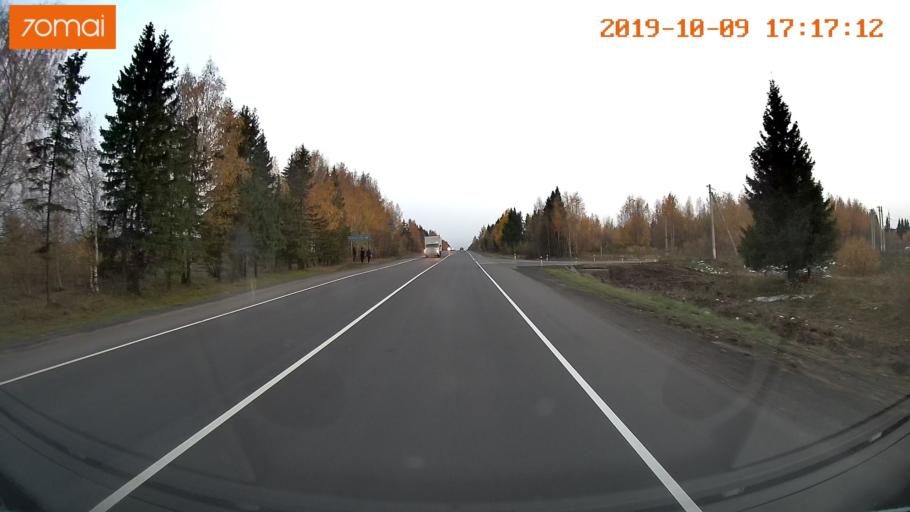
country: RU
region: Ivanovo
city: Furmanov
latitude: 57.2792
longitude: 41.1589
